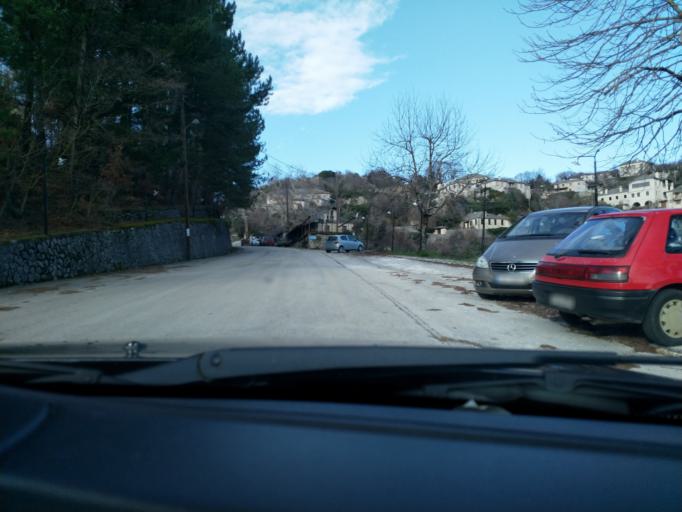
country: GR
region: Epirus
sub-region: Nomos Ioanninon
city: Asprangeloi
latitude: 39.8738
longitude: 20.7502
